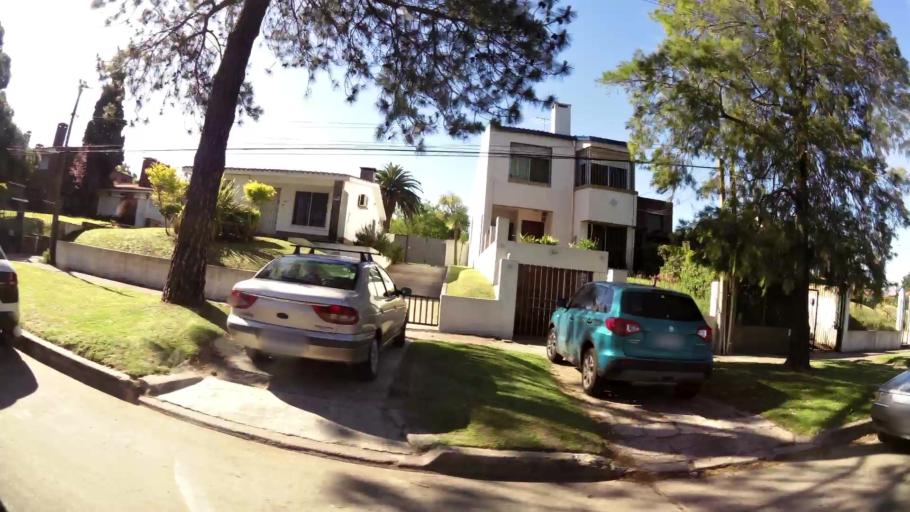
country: UY
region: Canelones
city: Paso de Carrasco
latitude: -34.8839
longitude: -56.0773
